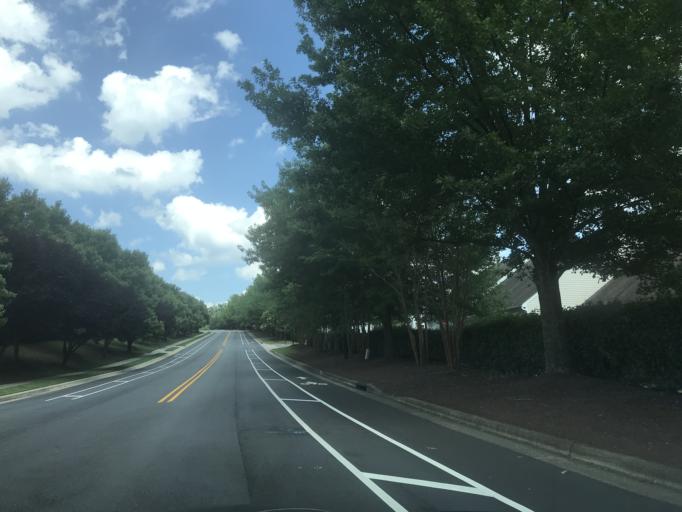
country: US
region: North Carolina
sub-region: Wake County
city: Cary
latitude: 35.8876
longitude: -78.7319
